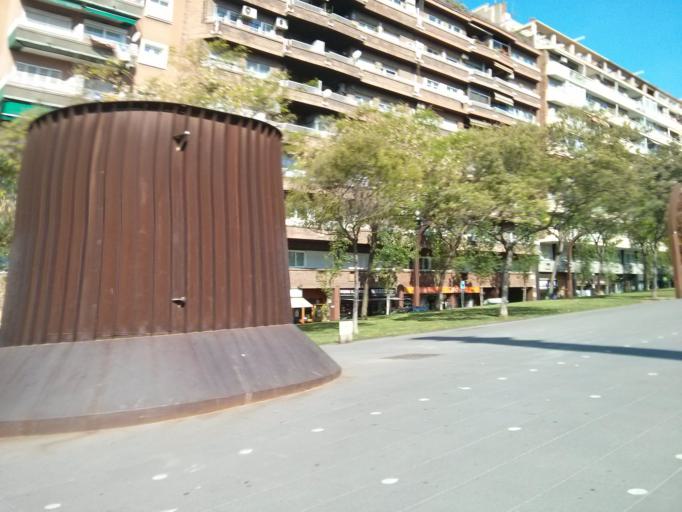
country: ES
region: Catalonia
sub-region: Provincia de Barcelona
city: les Corts
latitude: 41.3825
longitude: 2.1280
